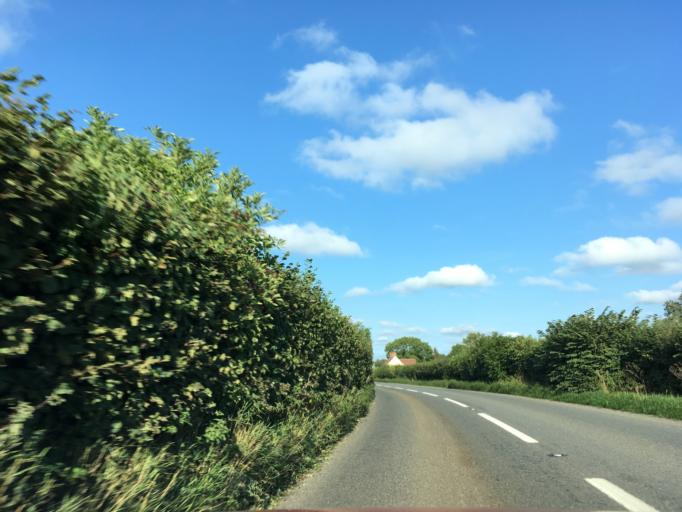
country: GB
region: England
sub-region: Somerset
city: Chilcompton
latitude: 51.2580
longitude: -2.5503
